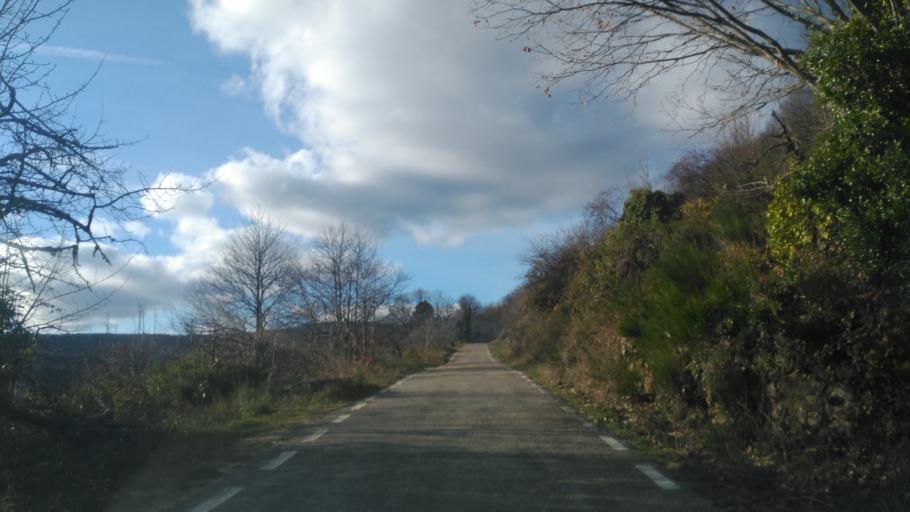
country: ES
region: Castille and Leon
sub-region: Provincia de Salamanca
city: San Martin del Castanar
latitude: 40.5156
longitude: -6.0497
